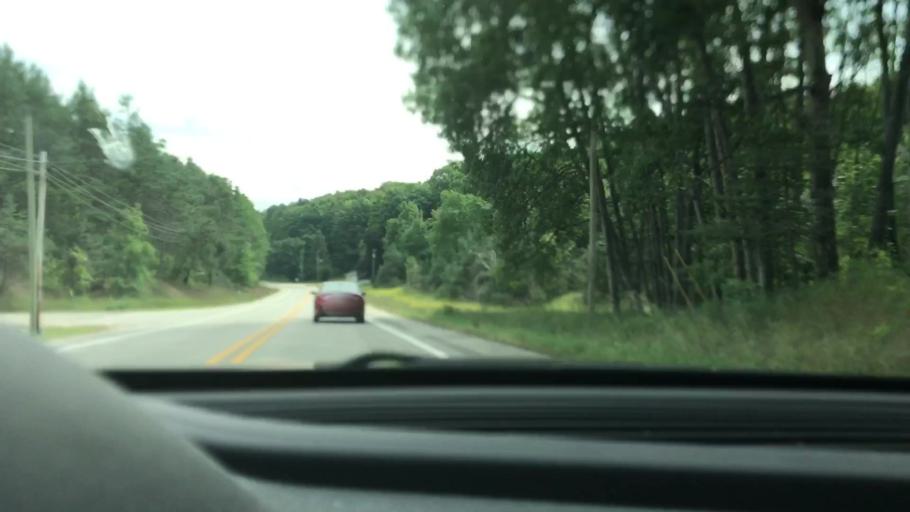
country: US
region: Michigan
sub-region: Antrim County
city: Bellaire
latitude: 45.0840
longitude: -85.2859
